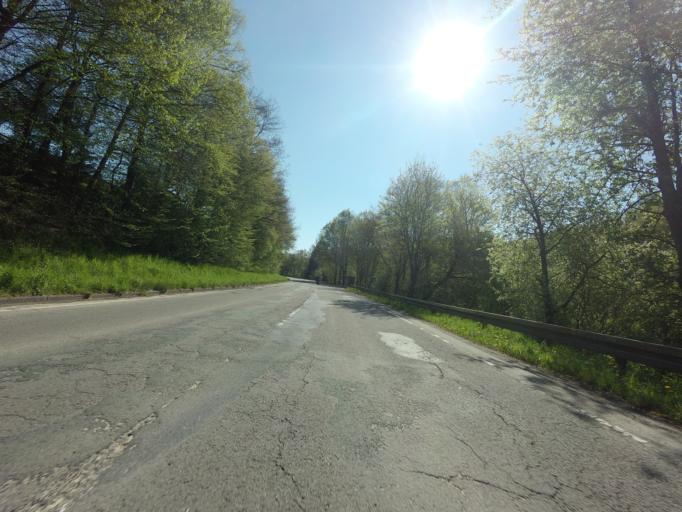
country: DE
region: North Rhine-Westphalia
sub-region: Regierungsbezirk Arnsberg
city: Drolshagen
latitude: 51.0772
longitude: 7.7637
